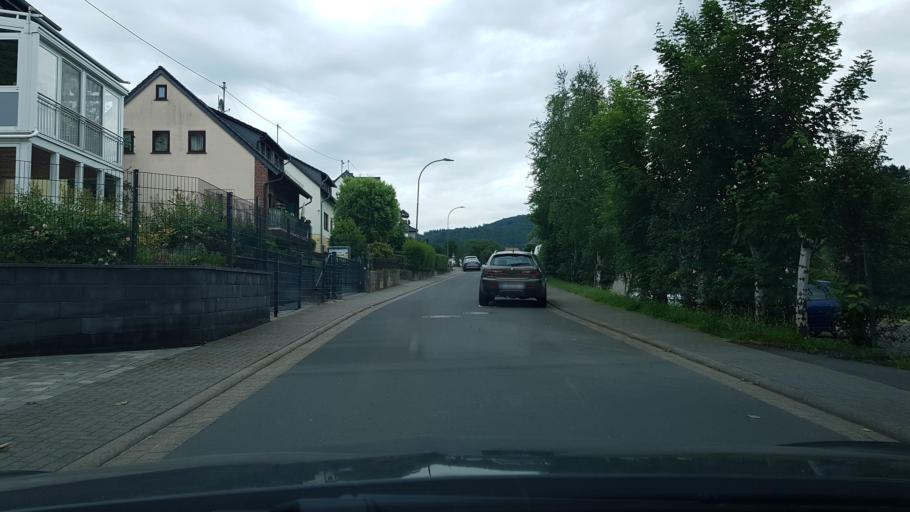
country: DE
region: Rheinland-Pfalz
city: Adenau
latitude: 50.3827
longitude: 6.9354
